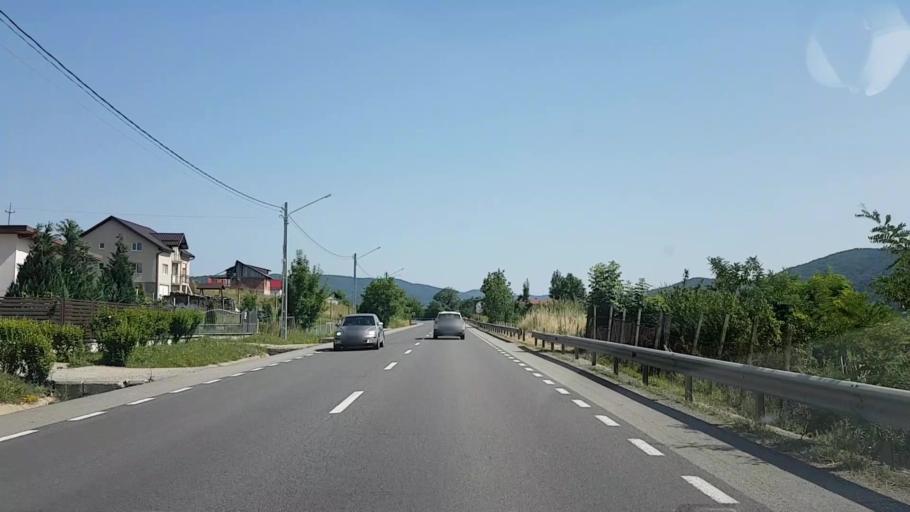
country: RO
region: Bistrita-Nasaud
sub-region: Comuna Sieu-Magherus
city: Sieu-Magherus
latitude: 47.0758
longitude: 24.3983
